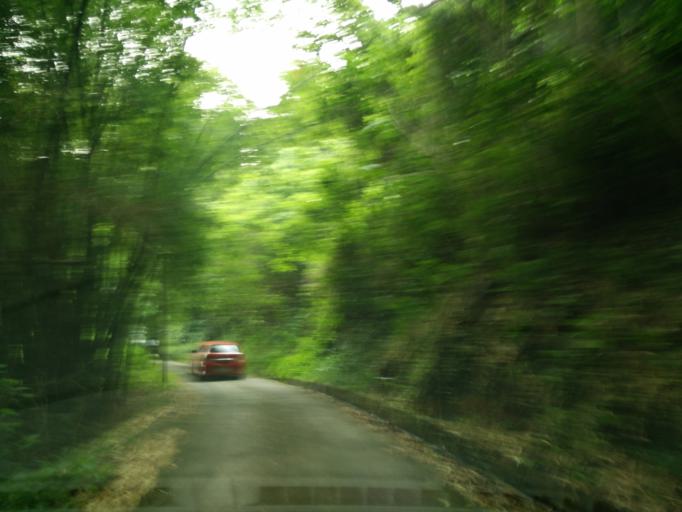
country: MQ
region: Martinique
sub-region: Martinique
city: Saint-Pierre
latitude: 14.7180
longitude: -61.1626
